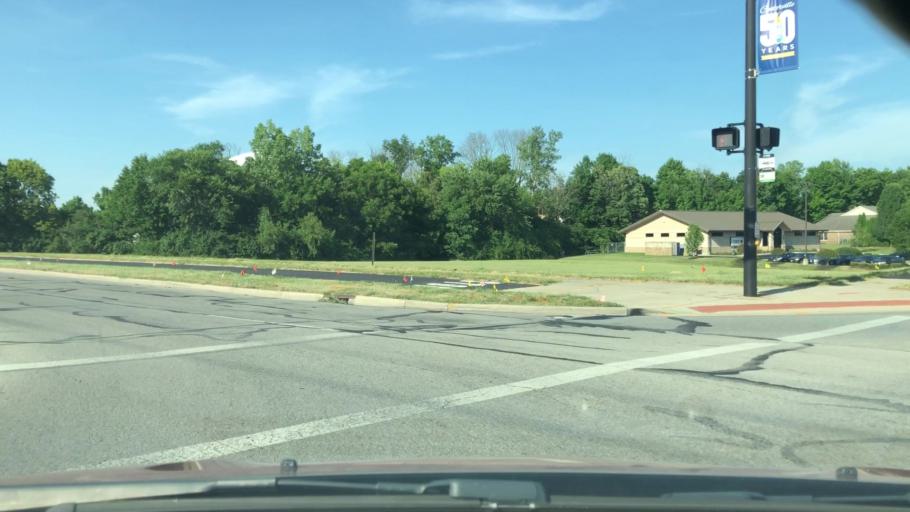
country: US
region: Ohio
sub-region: Montgomery County
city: Centerville
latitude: 39.6492
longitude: -84.1278
